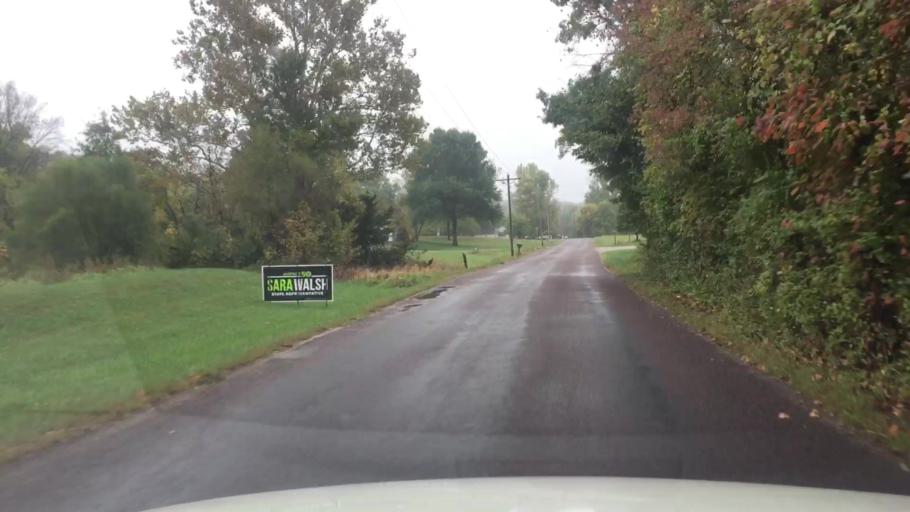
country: US
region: Missouri
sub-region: Boone County
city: Columbia
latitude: 38.8638
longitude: -92.3739
